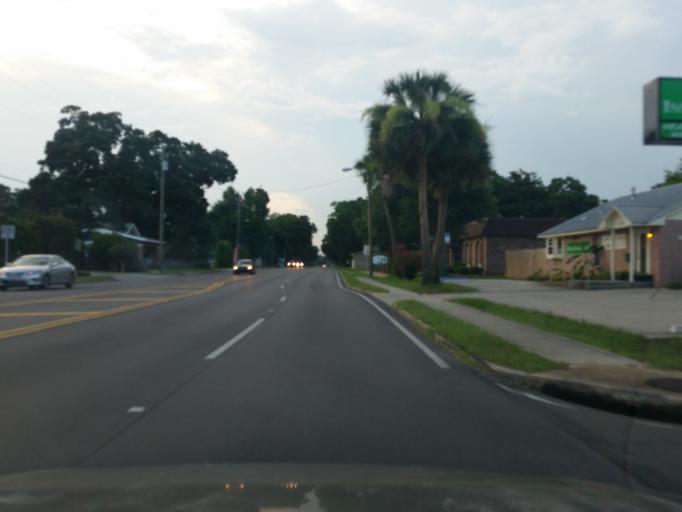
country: US
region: Florida
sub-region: Escambia County
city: Goulding
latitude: 30.4364
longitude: -87.2100
